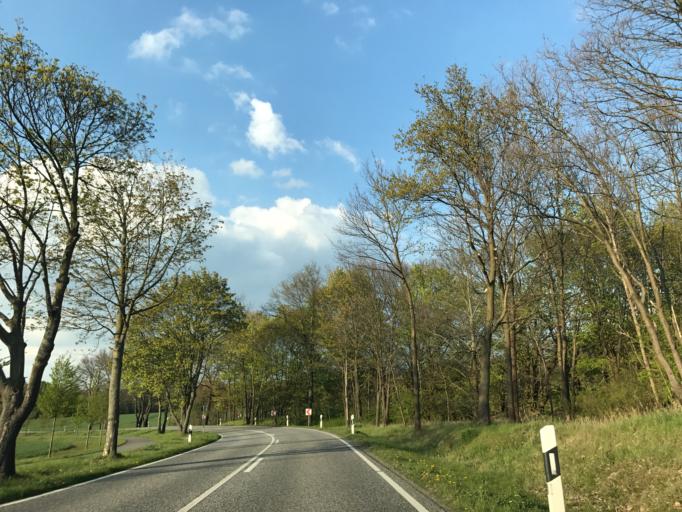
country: DE
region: Brandenburg
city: Wustermark
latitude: 52.5336
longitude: 12.9781
